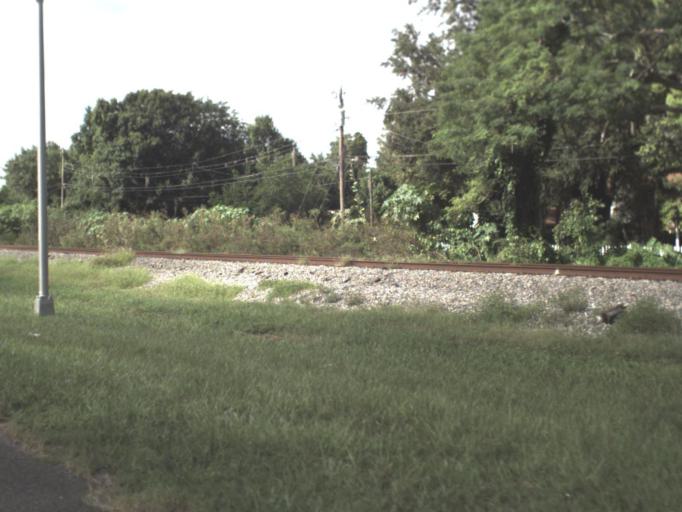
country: US
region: Florida
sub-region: Hillsborough County
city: Lutz
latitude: 28.1692
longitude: -82.4604
